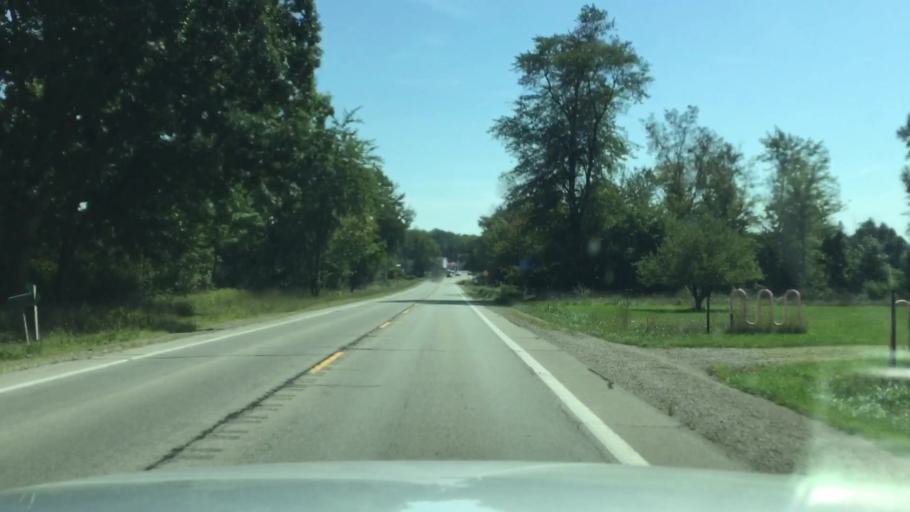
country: US
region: Michigan
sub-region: Lenawee County
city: Manitou Beach-Devils Lake
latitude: 42.0091
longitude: -84.2981
